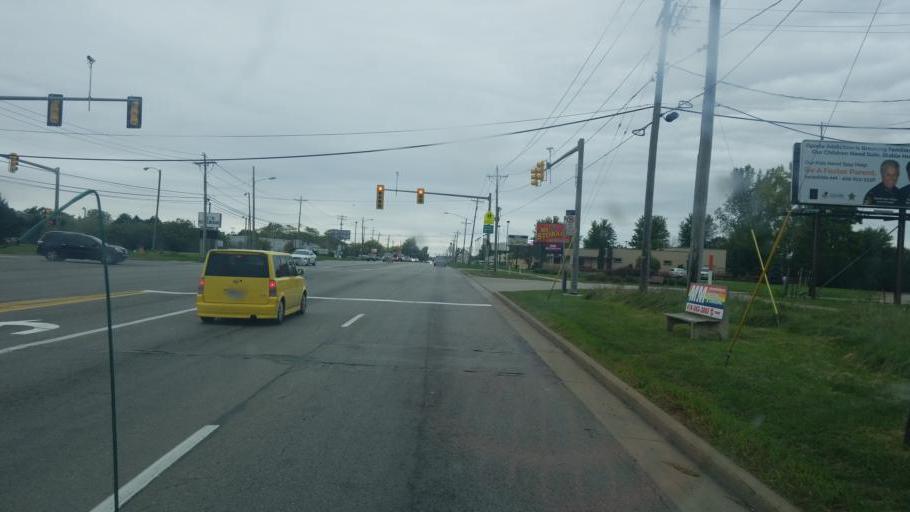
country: US
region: Ohio
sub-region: Lucas County
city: Ottawa Hills
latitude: 41.6265
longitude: -83.6644
